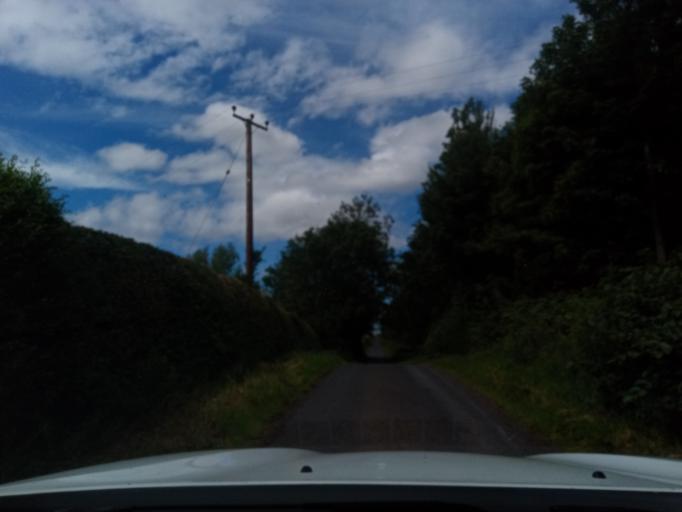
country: GB
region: Scotland
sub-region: The Scottish Borders
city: Jedburgh
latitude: 55.5621
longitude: -2.5371
